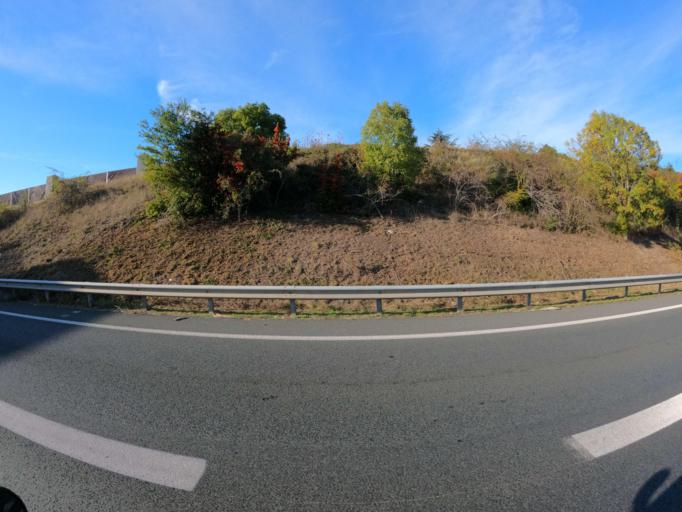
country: FR
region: Pays de la Loire
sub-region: Departement de Maine-et-Loire
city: Murs-Erigne
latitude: 47.3950
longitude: -0.5347
